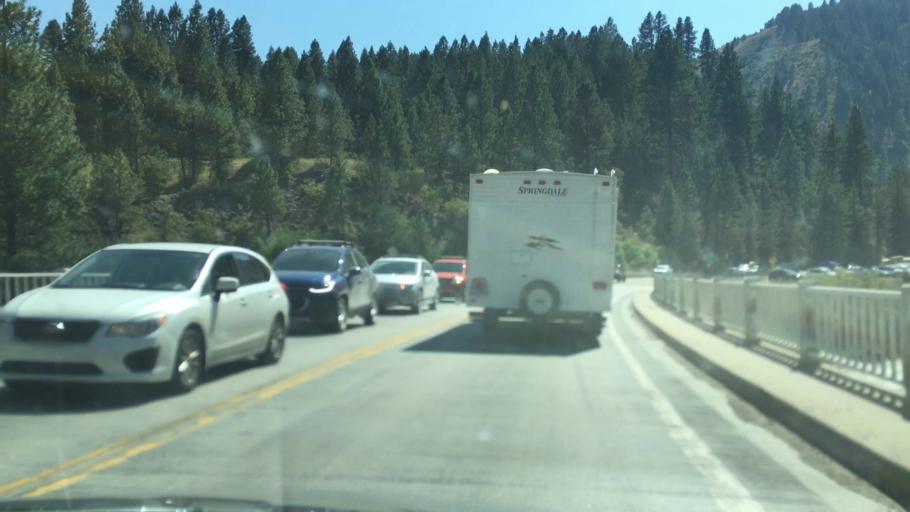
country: US
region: Idaho
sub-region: Boise County
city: Idaho City
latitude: 44.0844
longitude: -116.1148
